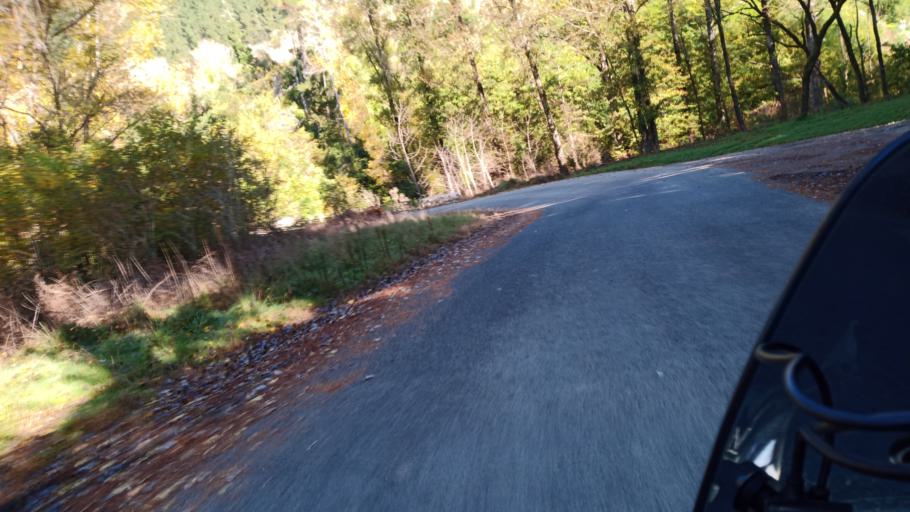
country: NZ
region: Hawke's Bay
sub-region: Wairoa District
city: Wairoa
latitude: -38.9206
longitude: 177.2417
